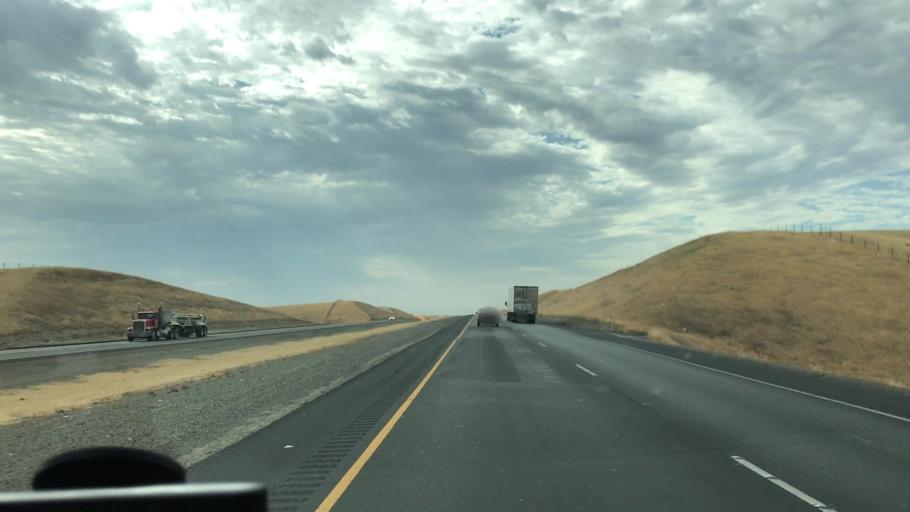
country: US
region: California
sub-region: San Joaquin County
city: Tracy
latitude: 37.6993
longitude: -121.5021
